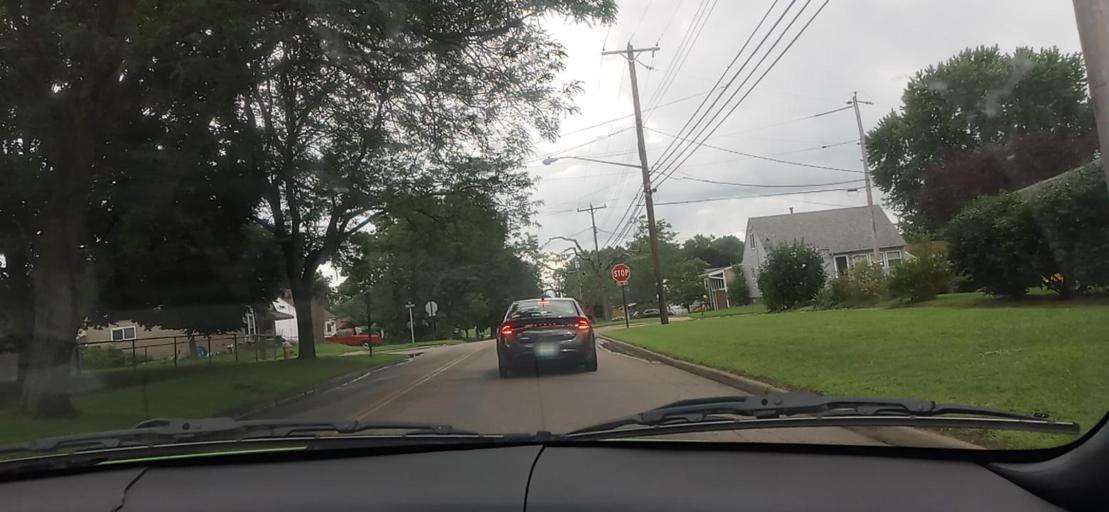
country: US
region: Ohio
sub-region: Summit County
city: Portage Lakes
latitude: 41.0248
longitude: -81.5599
